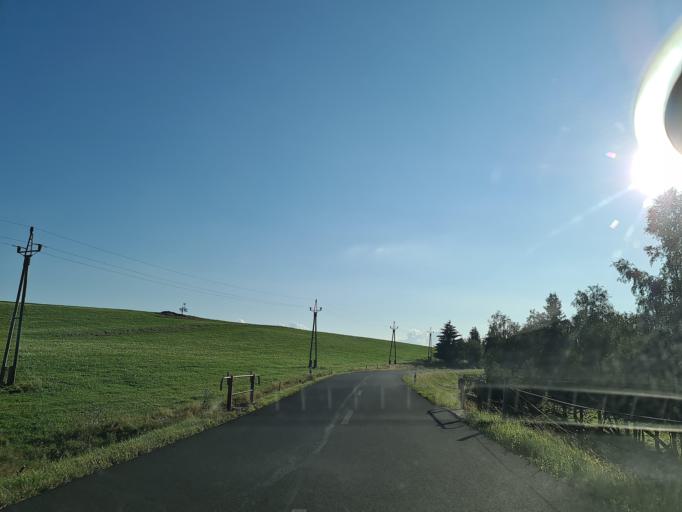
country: DE
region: Saxony
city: Deutschneudorf
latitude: 50.6233
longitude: 13.4940
